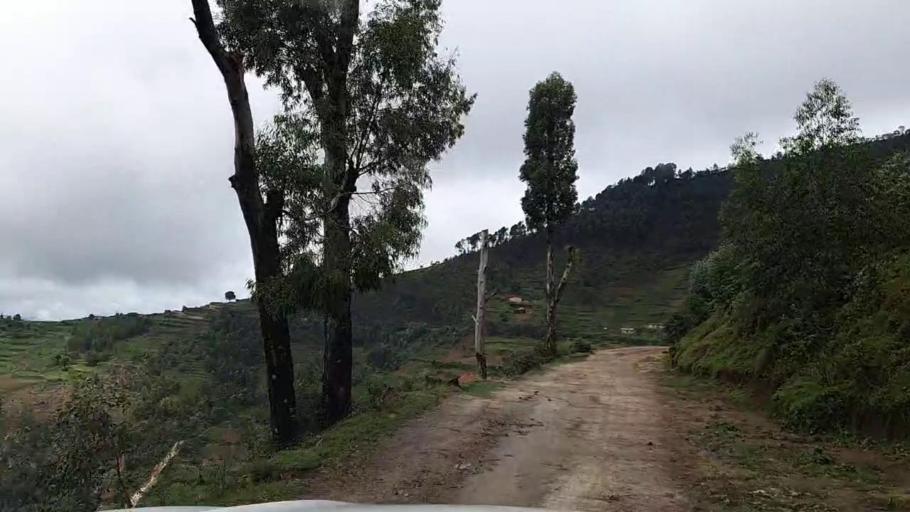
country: RW
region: Southern Province
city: Gikongoro
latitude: -2.3626
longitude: 29.4960
